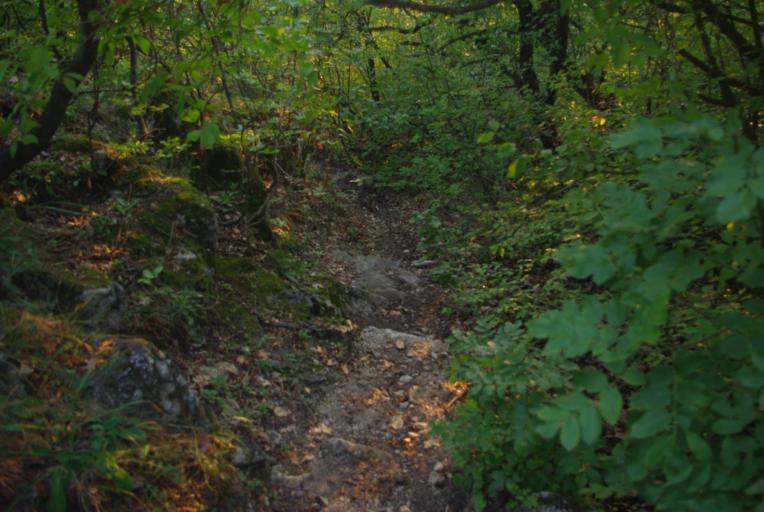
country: HU
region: Pest
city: Solymar
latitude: 47.5771
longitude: 18.9589
